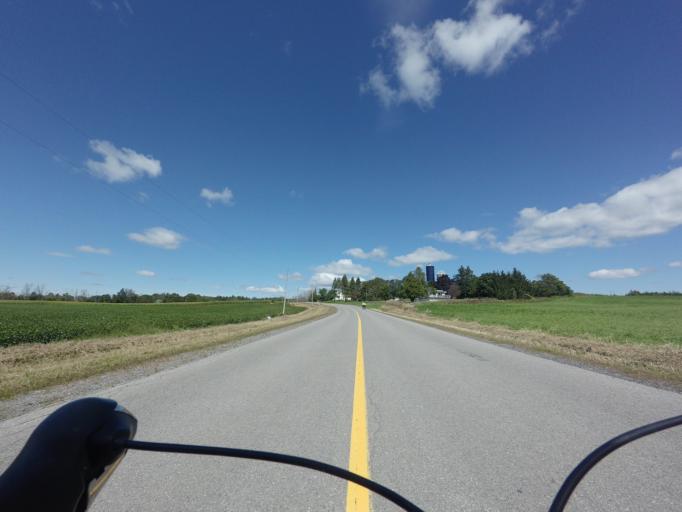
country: CA
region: Ontario
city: Bells Corners
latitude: 45.2591
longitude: -75.8093
